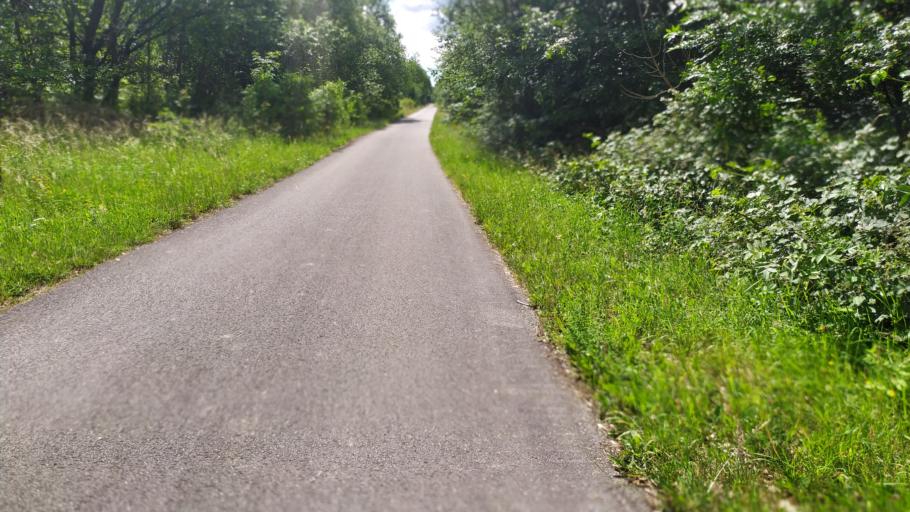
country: BE
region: Wallonia
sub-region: Province de Namur
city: Houyet
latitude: 50.1694
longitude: 5.0506
